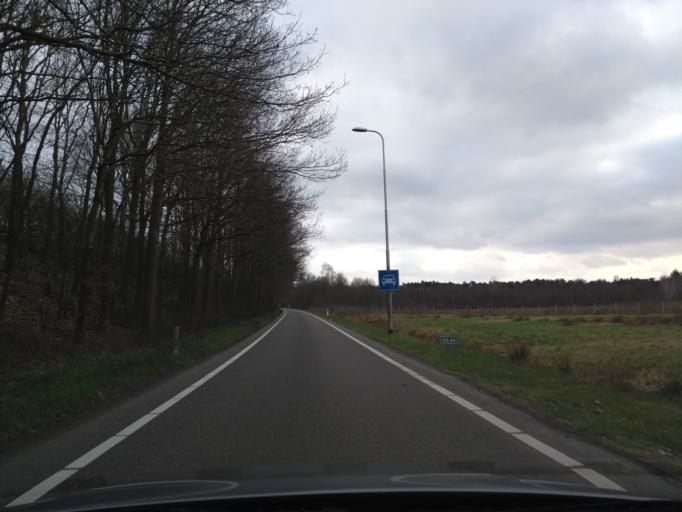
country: NL
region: Drenthe
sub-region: Gemeente Hoogeveen
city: Hoogeveen
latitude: 52.6022
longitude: 6.4072
